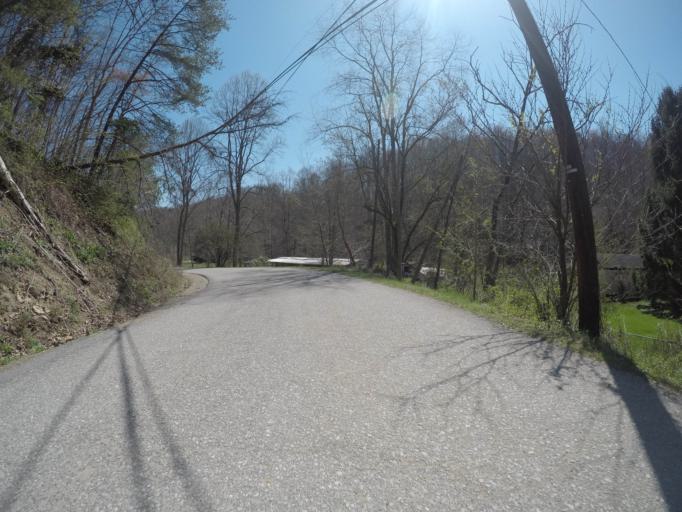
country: US
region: West Virginia
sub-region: Kanawha County
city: Charleston
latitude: 38.4157
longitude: -81.5770
